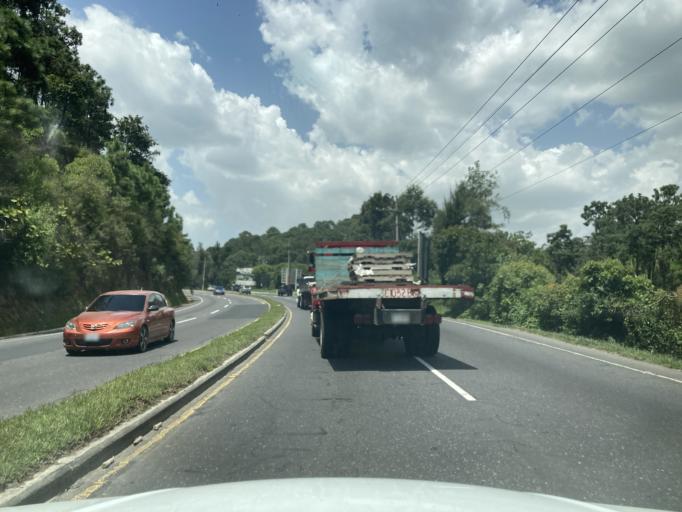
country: GT
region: Sacatepequez
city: Sumpango
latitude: 14.6410
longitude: -90.7429
